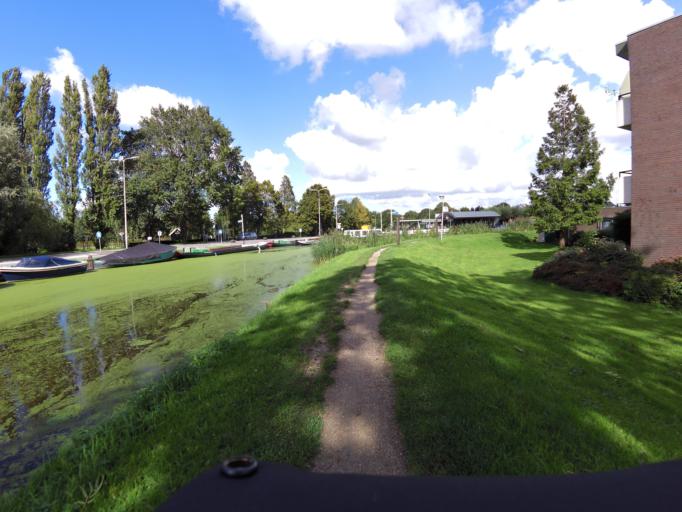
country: NL
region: South Holland
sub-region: Gemeente Delft
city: Delft
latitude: 51.9750
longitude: 4.3109
